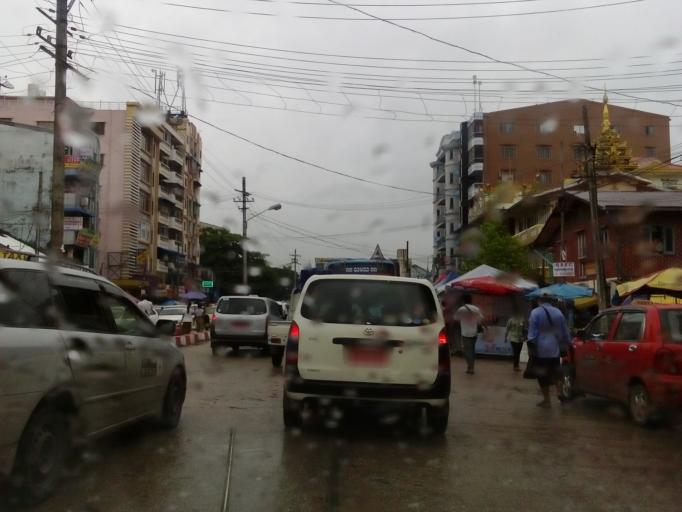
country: MM
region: Yangon
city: Yangon
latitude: 16.8082
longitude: 96.1764
